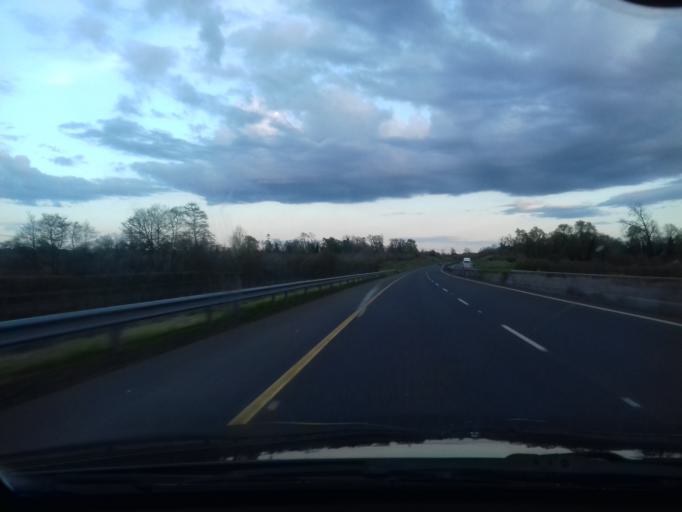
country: IE
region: Leinster
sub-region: An Mhi
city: Kells
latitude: 53.6978
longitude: -6.8334
